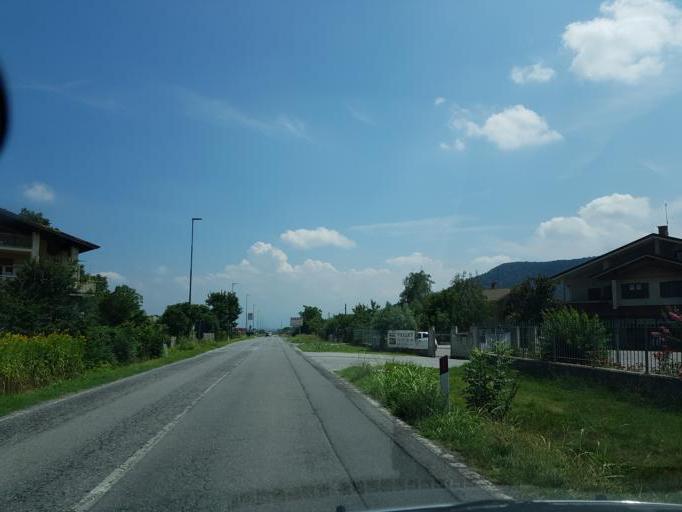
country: IT
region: Piedmont
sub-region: Provincia di Cuneo
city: Montemale di Cuneo
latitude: 44.4554
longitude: 7.3829
